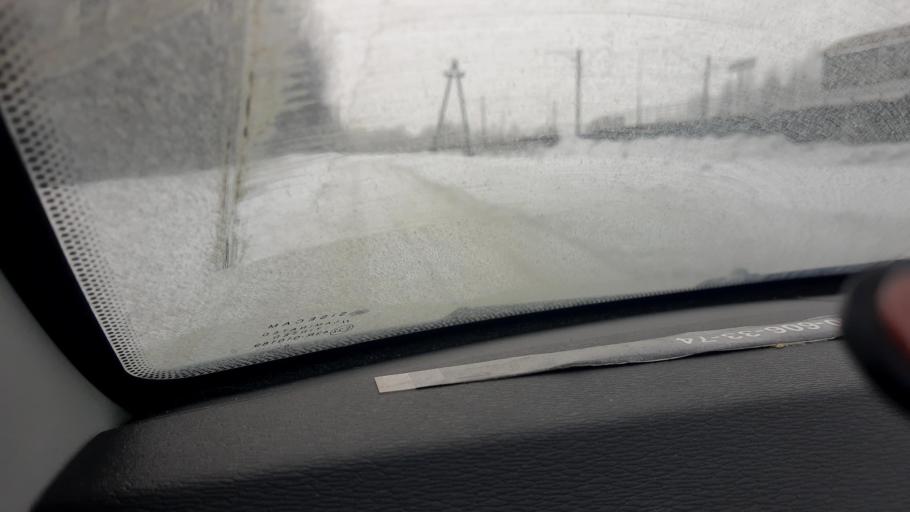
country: RU
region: Nizjnij Novgorod
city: Sitniki
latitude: 56.5217
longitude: 44.0509
